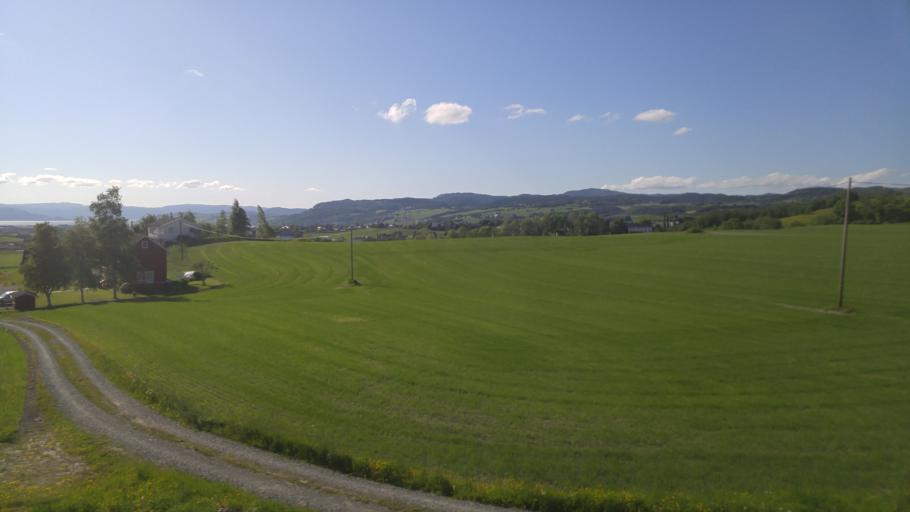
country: NO
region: Sor-Trondelag
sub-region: Melhus
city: Melhus
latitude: 63.3208
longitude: 10.3384
